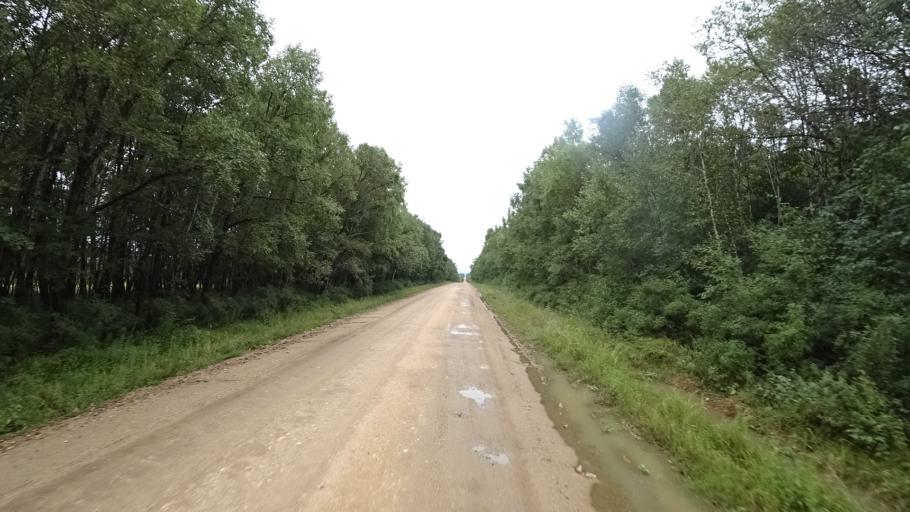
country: RU
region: Primorskiy
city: Ivanovka
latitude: 44.0324
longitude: 132.5313
